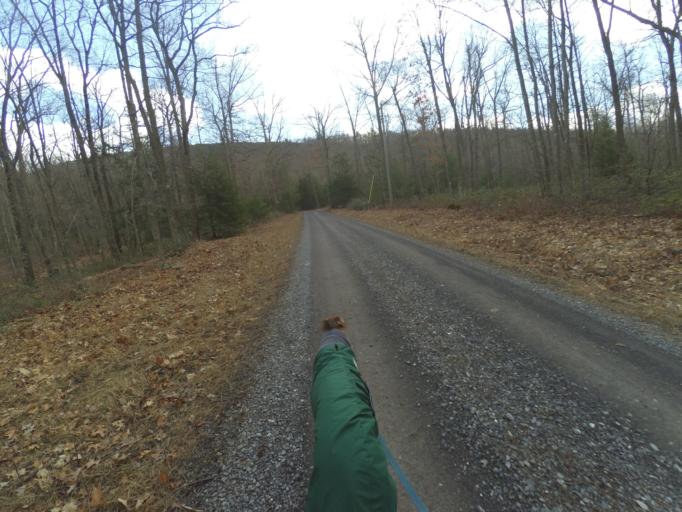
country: US
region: Pennsylvania
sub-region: Centre County
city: Boalsburg
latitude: 40.7553
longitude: -77.7087
